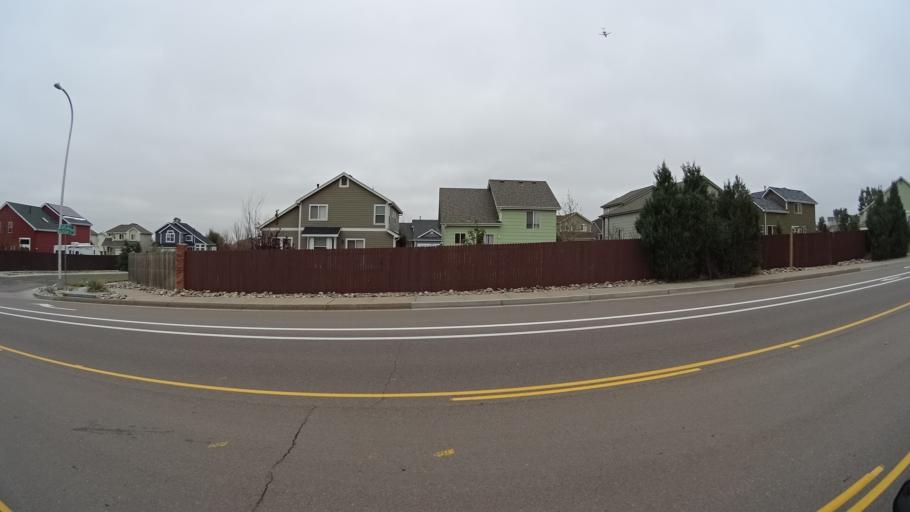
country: US
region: Colorado
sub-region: El Paso County
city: Cimarron Hills
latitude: 38.9064
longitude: -104.7166
